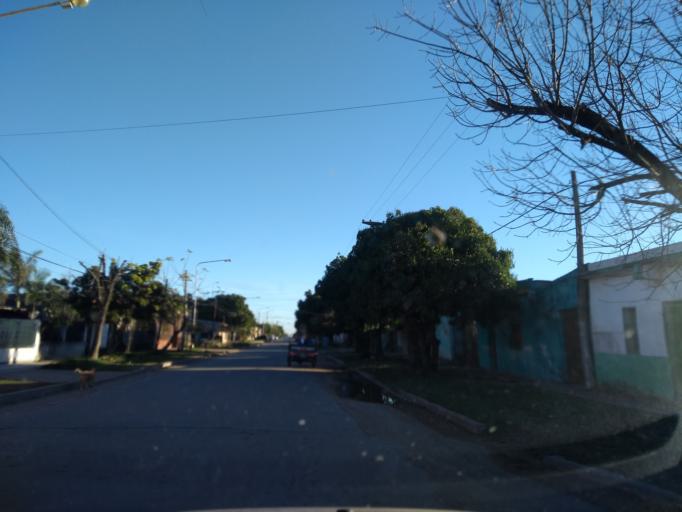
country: AR
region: Chaco
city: Barranqueras
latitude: -27.4894
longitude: -58.9469
